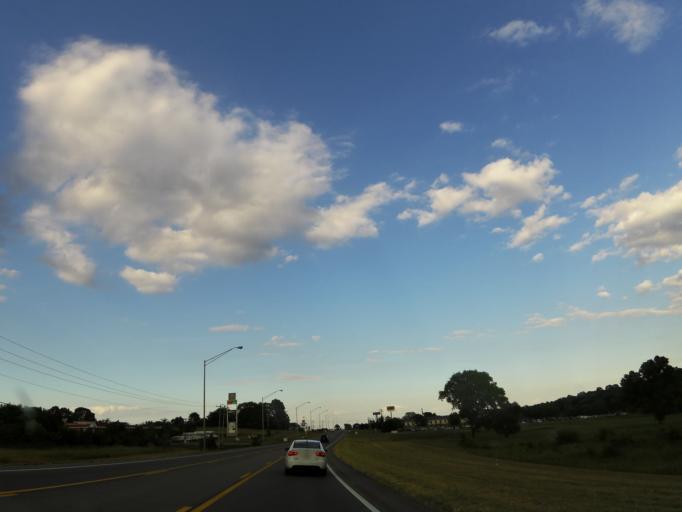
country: US
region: Tennessee
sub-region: Maury County
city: Spring Hill
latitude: 35.6426
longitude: -86.9039
